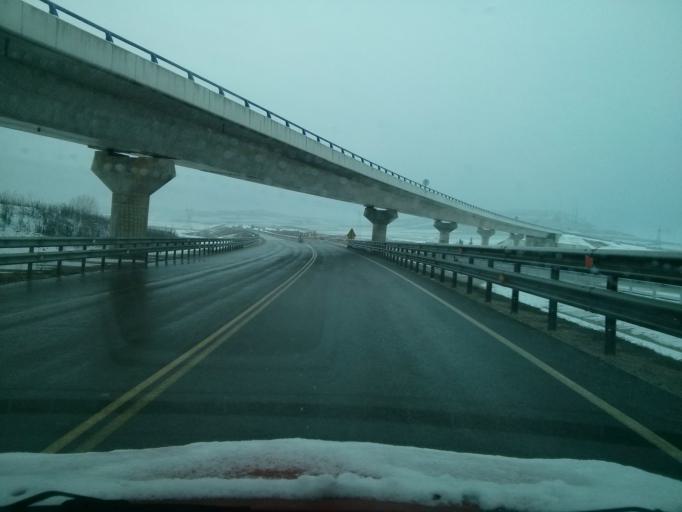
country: ES
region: Castille and Leon
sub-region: Provincia de Burgos
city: Sotragero
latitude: 42.3861
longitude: -3.6870
